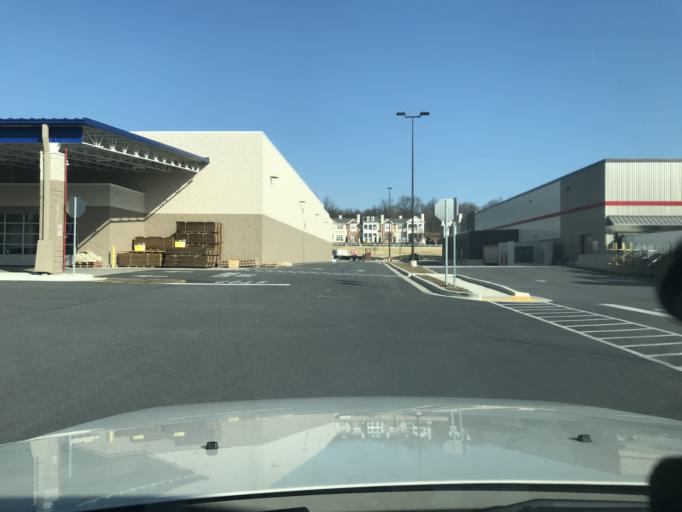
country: US
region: Maryland
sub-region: Baltimore County
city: Owings Mills
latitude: 39.4069
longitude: -76.7909
